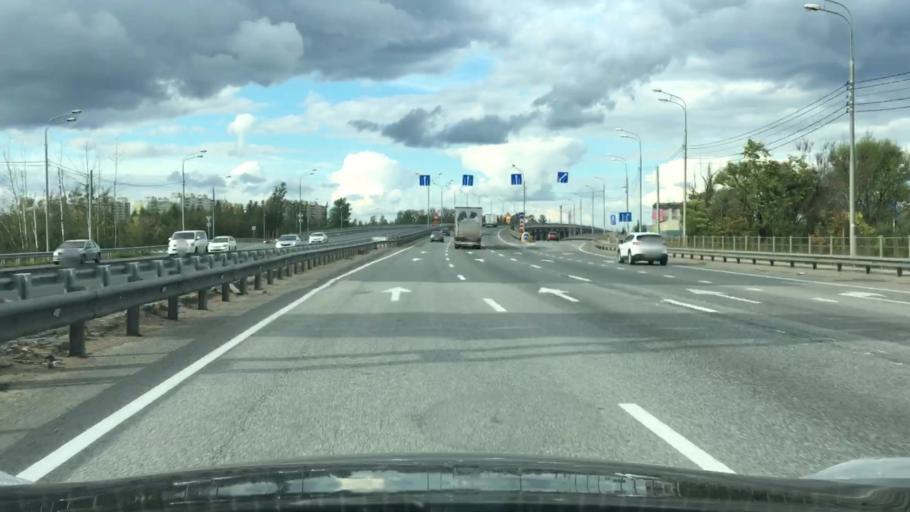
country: RU
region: Tverskaya
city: Tver
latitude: 56.8386
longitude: 35.7944
